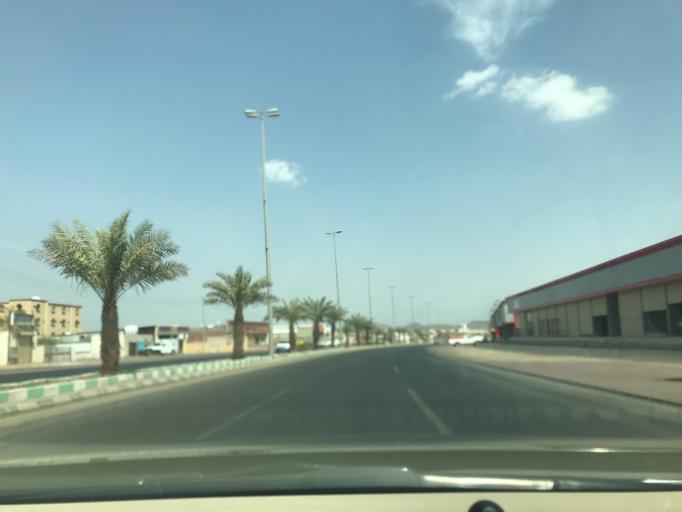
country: SA
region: Makkah
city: Al Jumum
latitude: 21.6237
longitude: 39.6813
